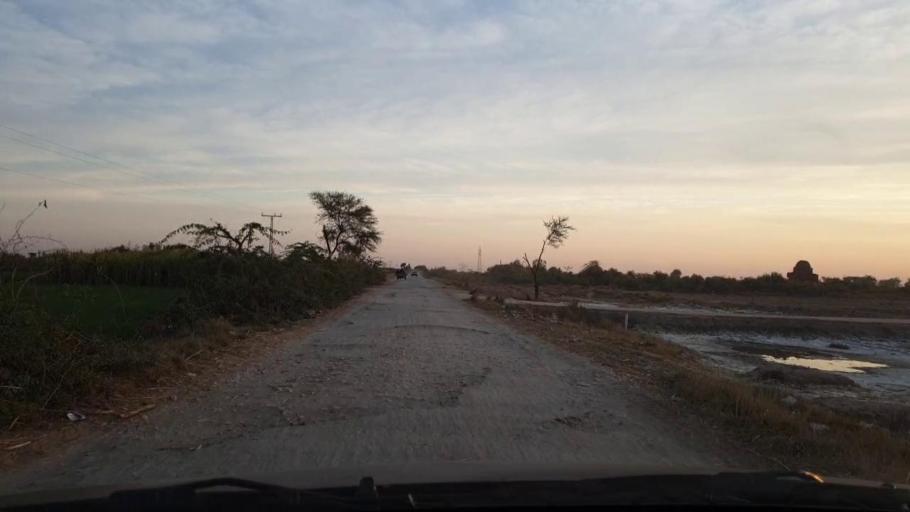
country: PK
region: Sindh
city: Khadro
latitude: 26.1180
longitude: 68.7962
